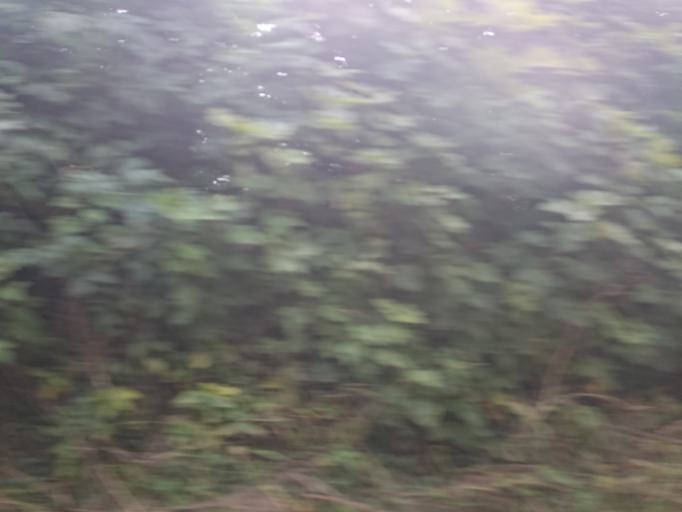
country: GB
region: England
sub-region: Gloucestershire
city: Coates
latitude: 51.7655
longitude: -2.0393
